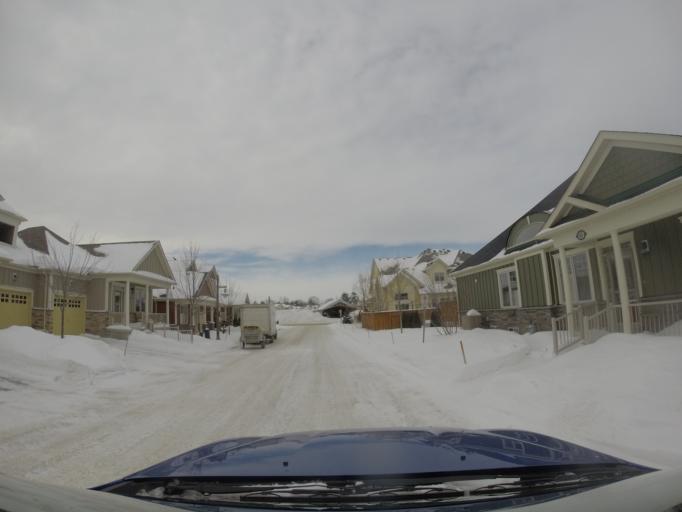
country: CA
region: Ontario
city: Wasaga Beach
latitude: 44.5285
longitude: -80.0070
